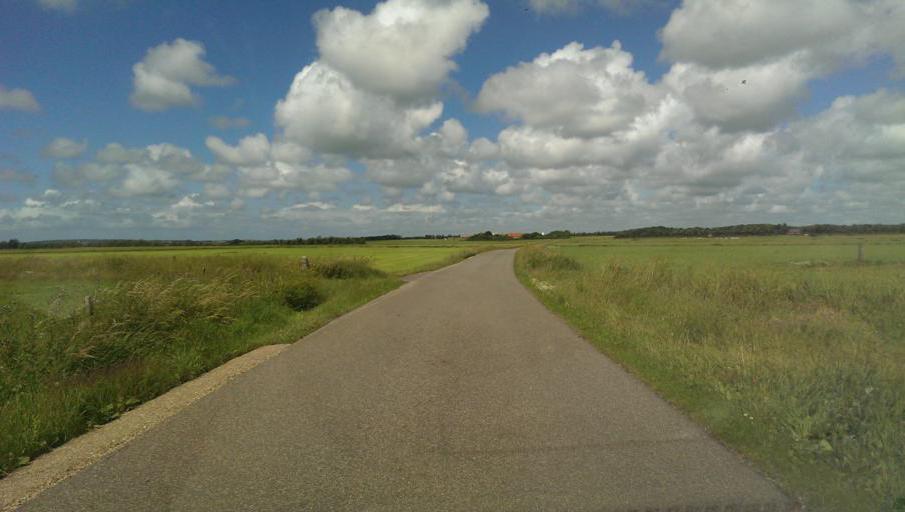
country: DK
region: Central Jutland
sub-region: Holstebro Kommune
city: Ulfborg
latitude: 56.2368
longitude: 8.2358
